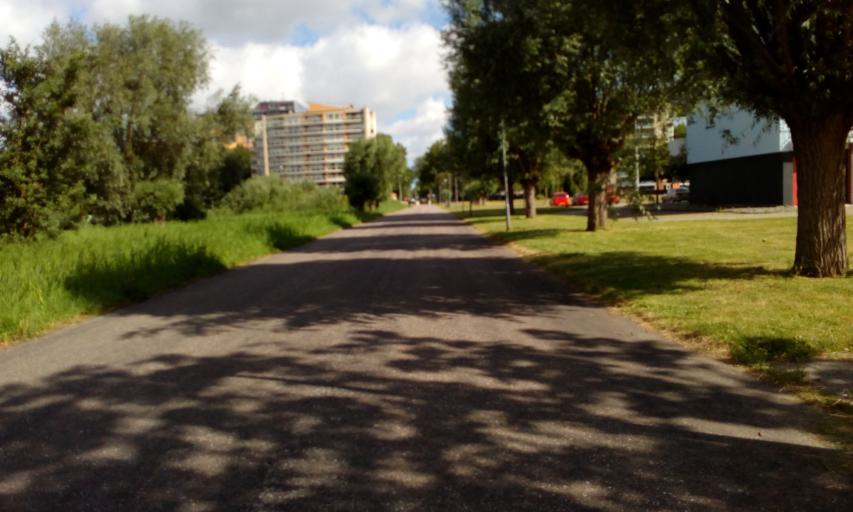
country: NL
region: South Holland
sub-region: Gemeente Rotterdam
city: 's-Gravenland
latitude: 51.9370
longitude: 4.5483
